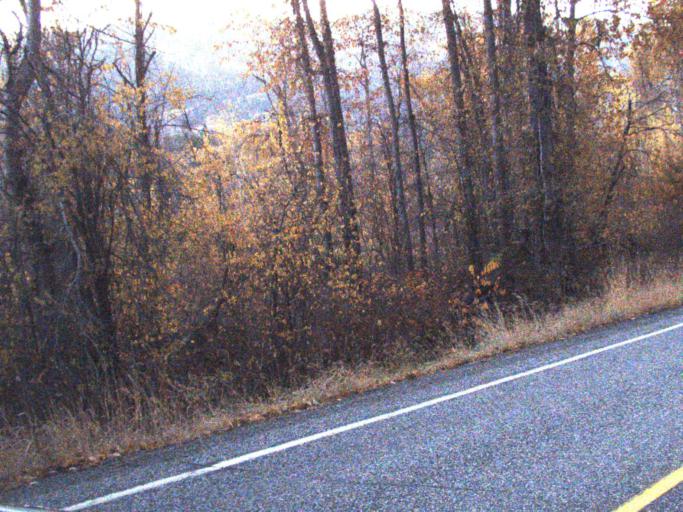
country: US
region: Washington
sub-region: Ferry County
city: Republic
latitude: 48.3339
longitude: -118.7479
